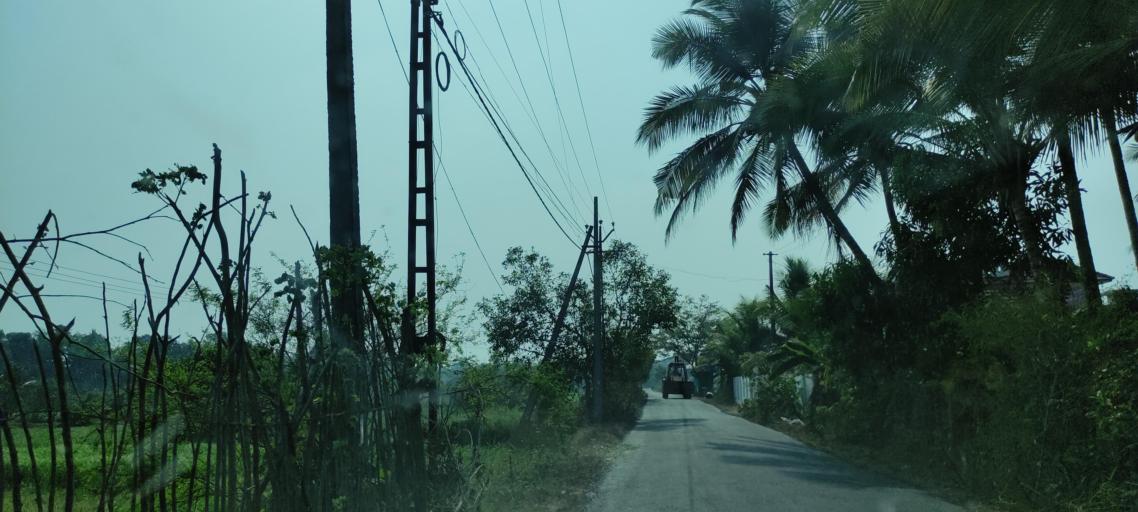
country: IN
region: Kerala
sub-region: Pattanamtitta
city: Tiruvalla
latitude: 9.3609
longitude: 76.5003
